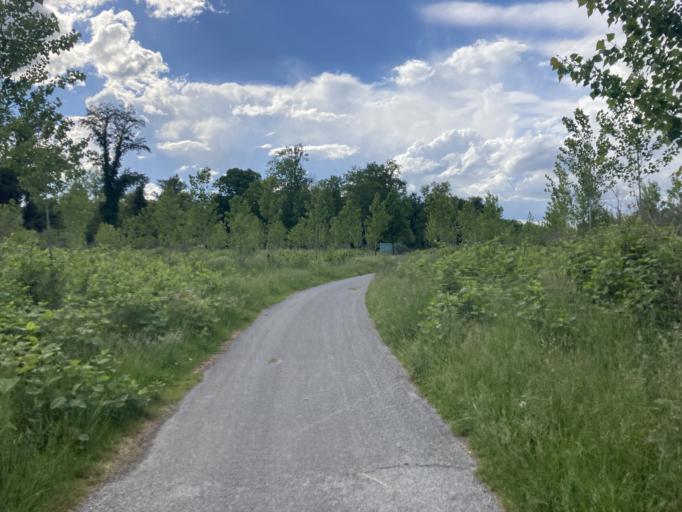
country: FR
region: Aquitaine
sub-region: Departement des Pyrenees-Atlantiques
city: Arbus
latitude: 43.3469
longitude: -0.5091
